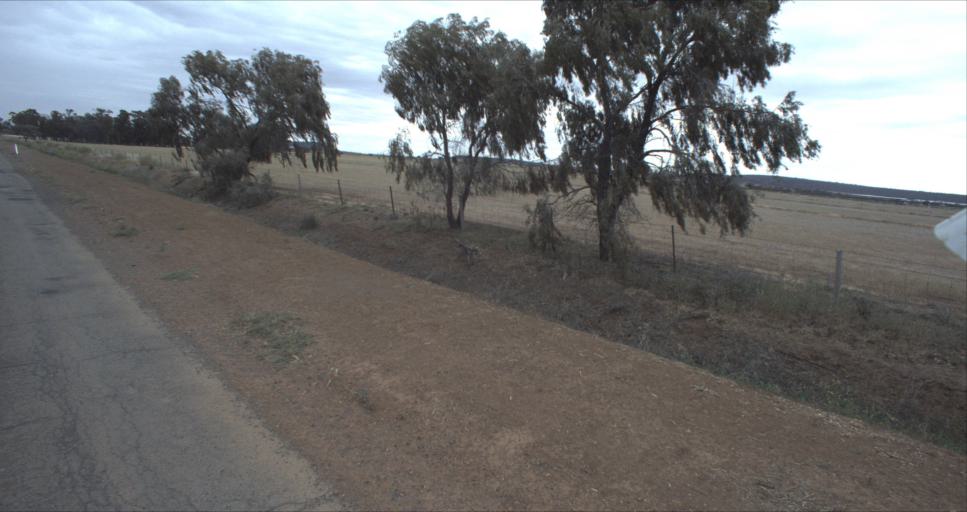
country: AU
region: New South Wales
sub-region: Leeton
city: Leeton
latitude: -34.4121
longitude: 146.3401
